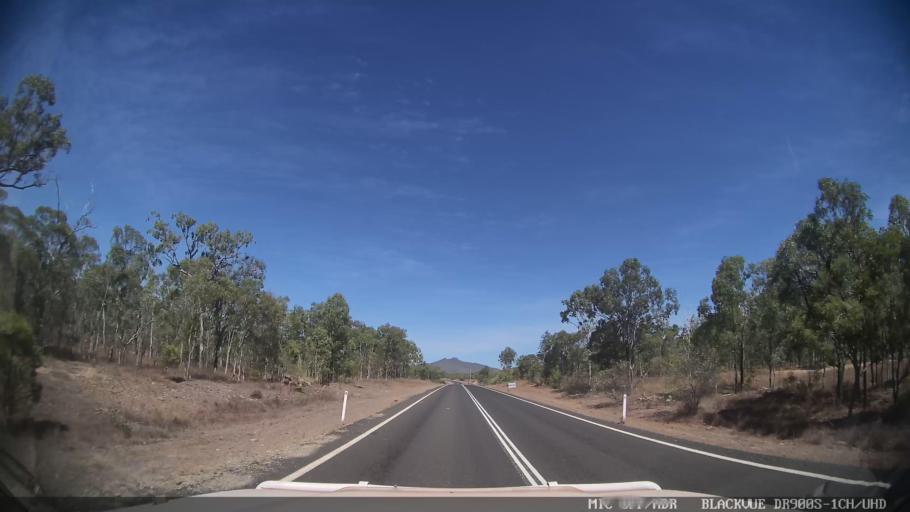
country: AU
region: Queensland
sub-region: Cook
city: Cooktown
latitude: -15.7044
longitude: 144.6086
